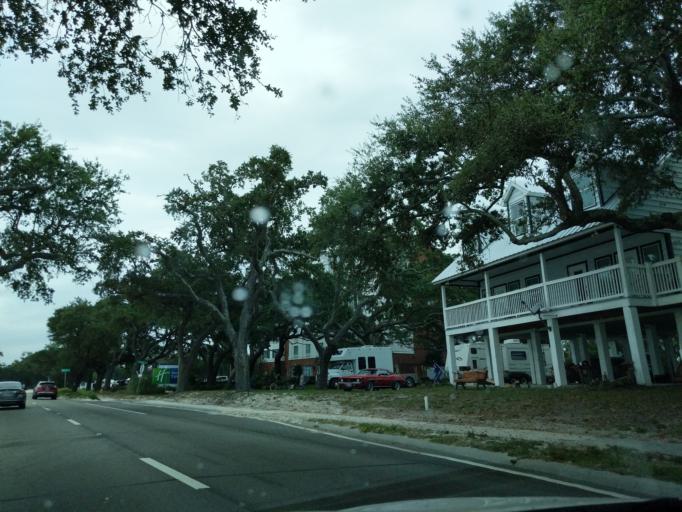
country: US
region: Mississippi
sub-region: Harrison County
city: Long Beach
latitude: 30.3437
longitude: -89.1533
